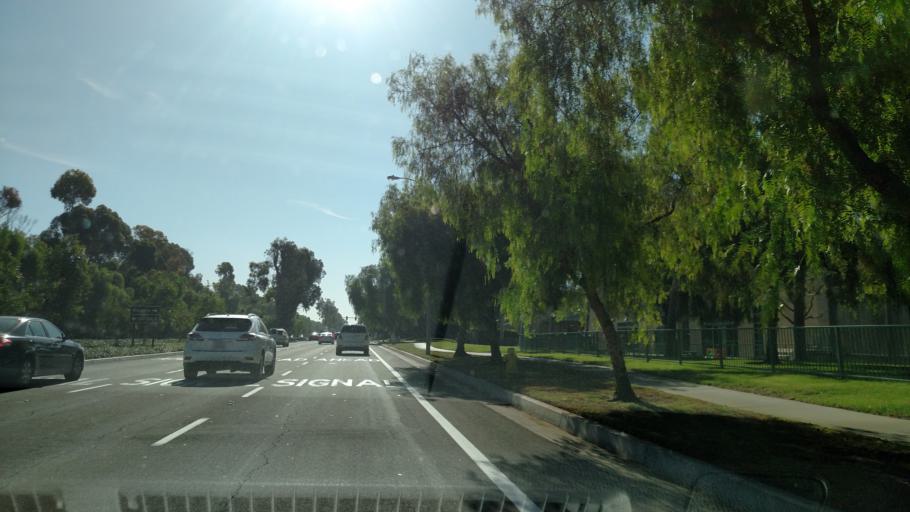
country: US
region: California
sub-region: Orange County
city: Irvine
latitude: 33.6762
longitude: -117.7741
